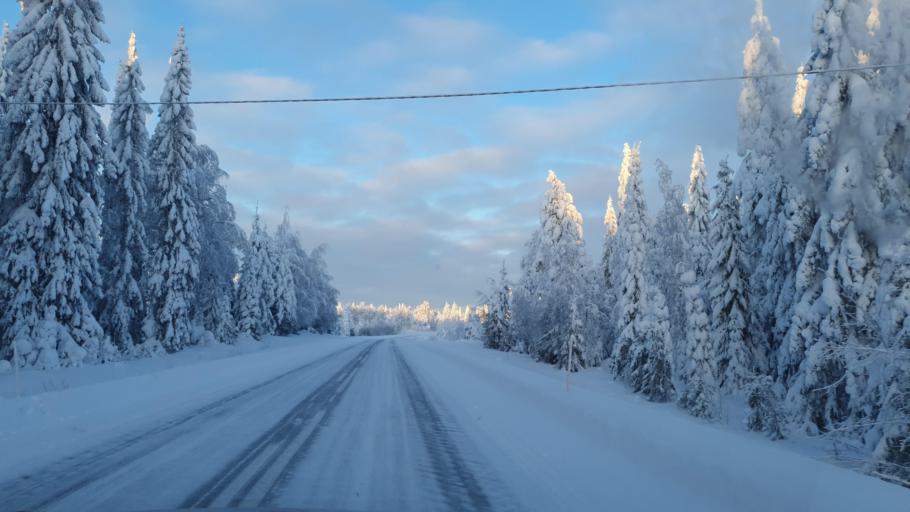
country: FI
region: Kainuu
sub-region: Kajaani
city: Vuokatti
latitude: 64.2468
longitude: 28.2309
